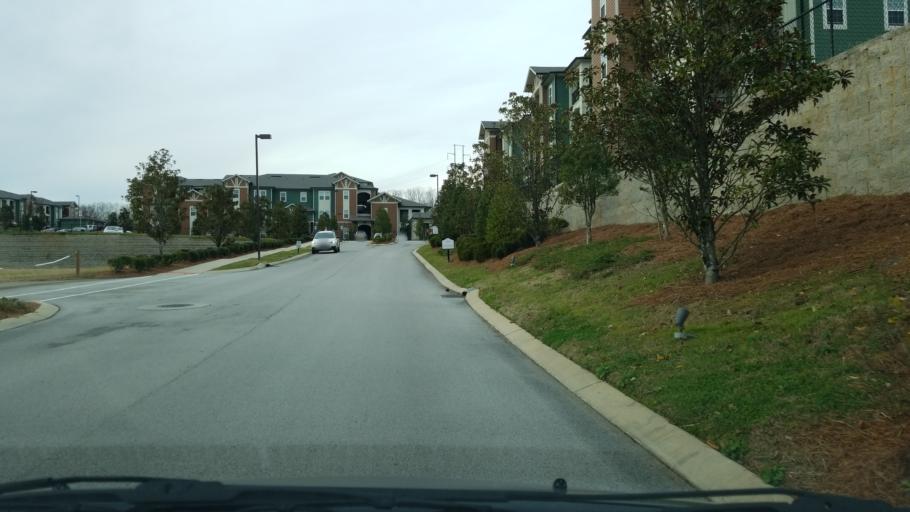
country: US
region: Tennessee
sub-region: Hamilton County
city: Collegedale
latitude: 35.0656
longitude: -85.0733
